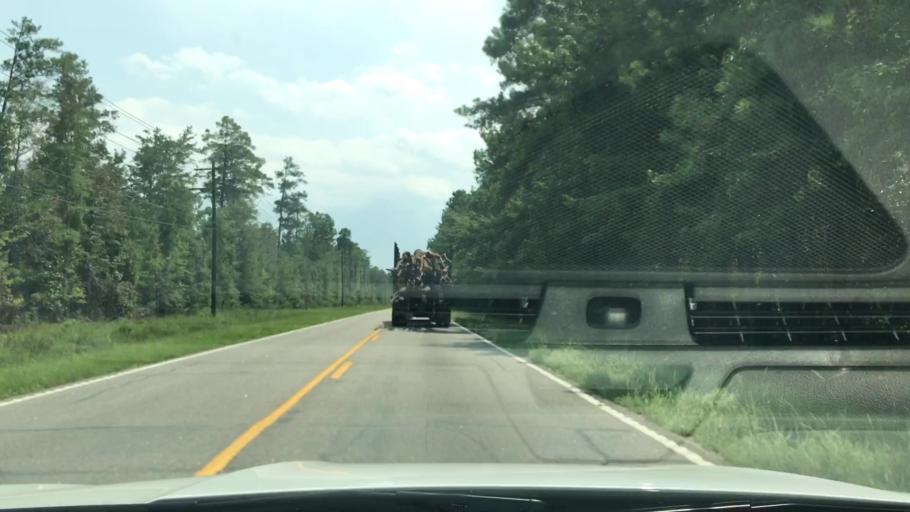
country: US
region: South Carolina
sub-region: Georgetown County
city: Georgetown
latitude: 33.4495
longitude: -79.2791
